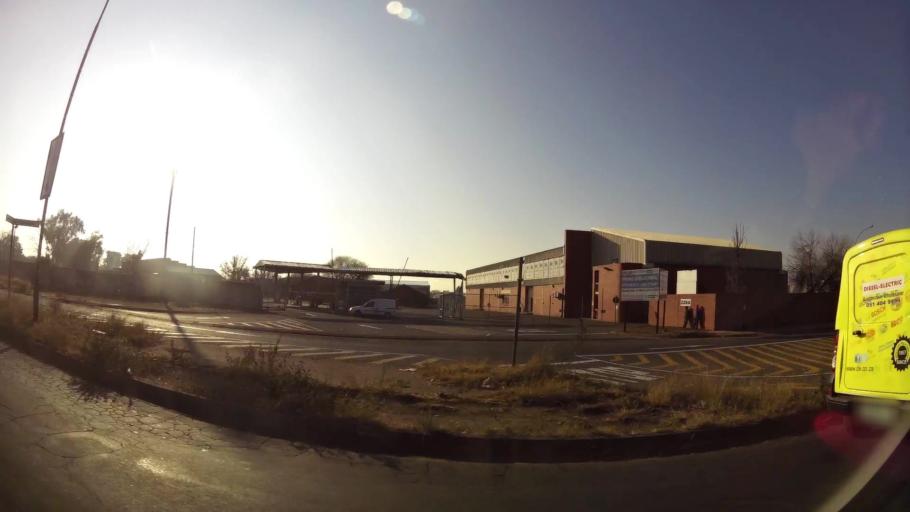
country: ZA
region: Orange Free State
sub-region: Mangaung Metropolitan Municipality
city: Bloemfontein
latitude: -29.1415
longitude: 26.2156
